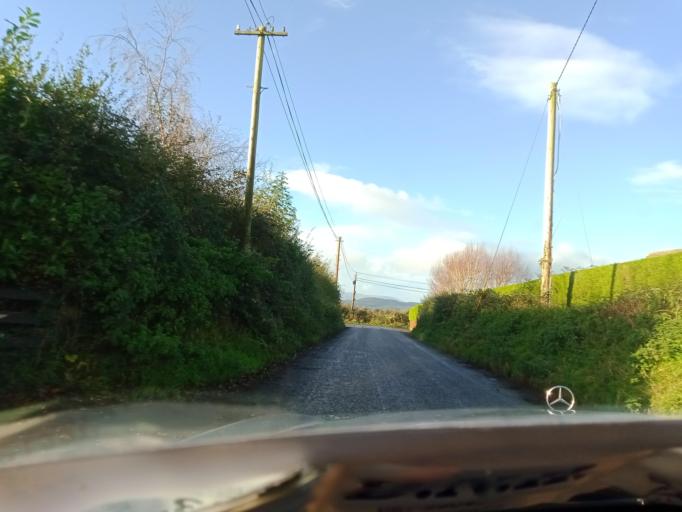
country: IE
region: Leinster
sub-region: Kilkenny
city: Mooncoin
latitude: 52.2756
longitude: -7.2167
